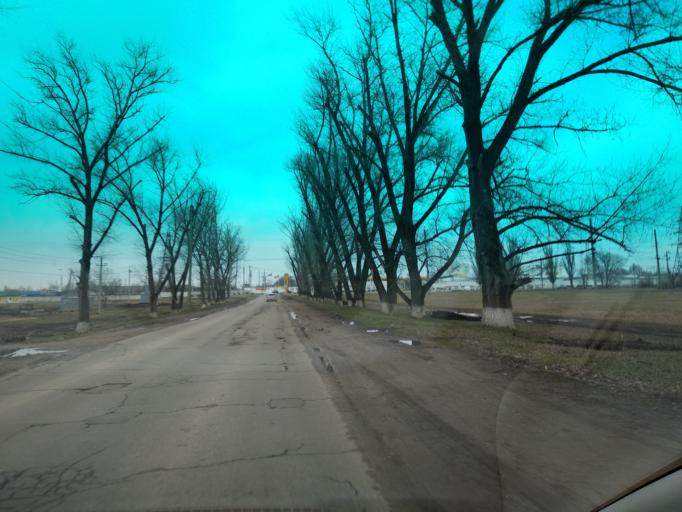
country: RU
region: Krasnodarskiy
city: Tikhoretsk
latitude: 45.8385
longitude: 40.1259
